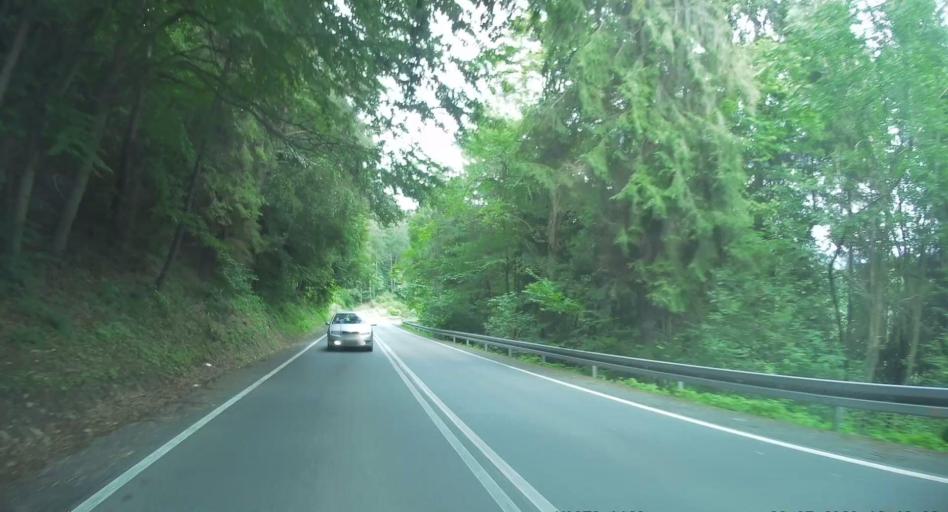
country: PL
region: Lesser Poland Voivodeship
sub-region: Powiat nowosadecki
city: Muszyna
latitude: 49.3466
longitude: 20.8047
